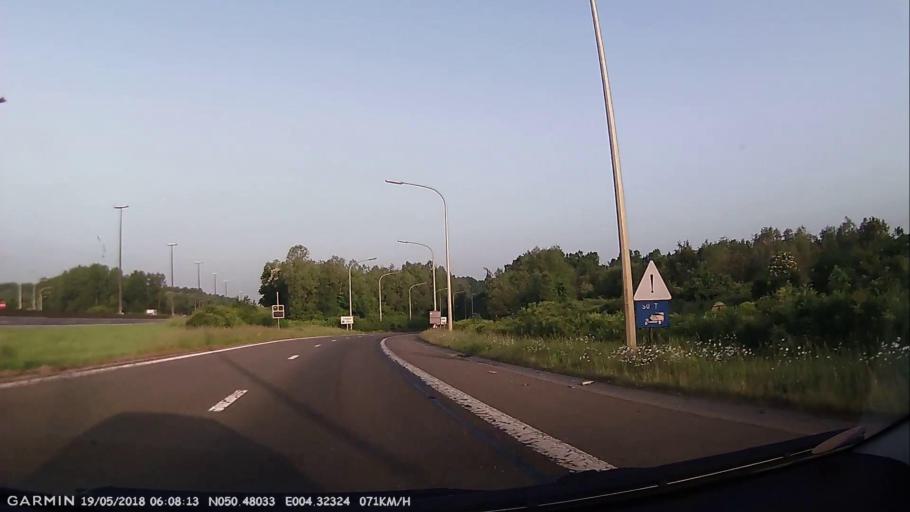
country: BE
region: Wallonia
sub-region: Province du Hainaut
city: Chapelle-lez-Herlaimont
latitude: 50.4804
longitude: 4.3230
